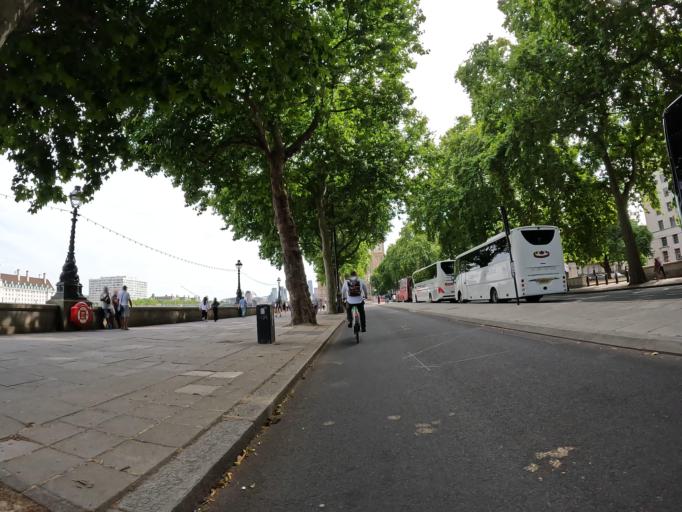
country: GB
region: England
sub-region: Greater London
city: Bromley
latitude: 51.4183
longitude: 0.0208
